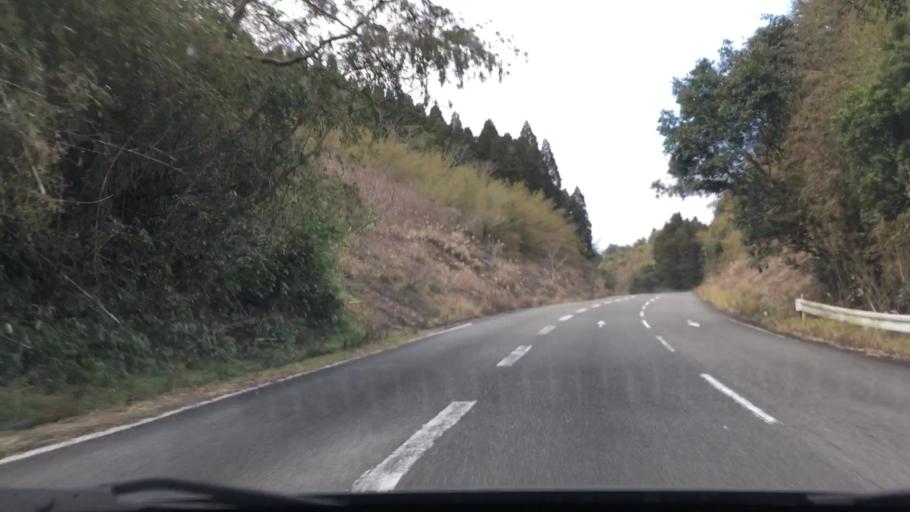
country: JP
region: Miyazaki
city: Nichinan
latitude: 31.6357
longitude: 131.3368
